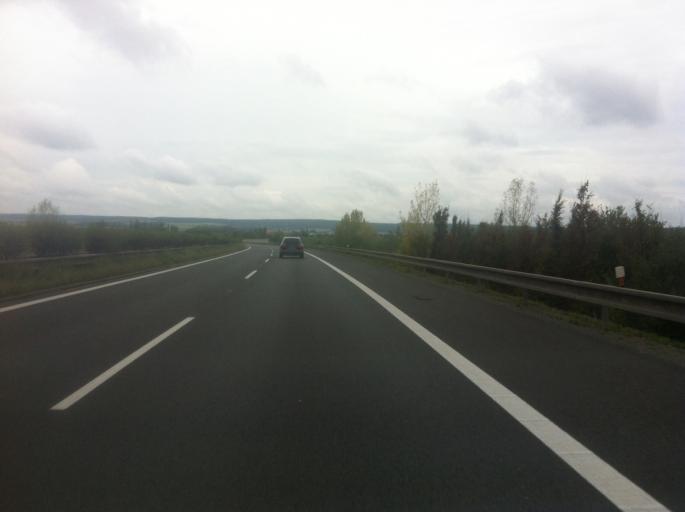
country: CZ
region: Plzensky
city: Nyrany
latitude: 49.7098
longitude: 13.1730
